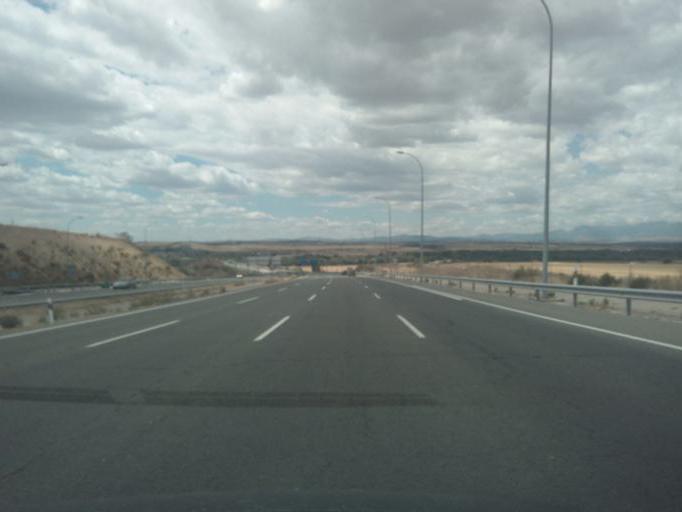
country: ES
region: Madrid
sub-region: Provincia de Madrid
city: Paracuellos de Jarama
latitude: 40.5434
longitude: -3.5428
